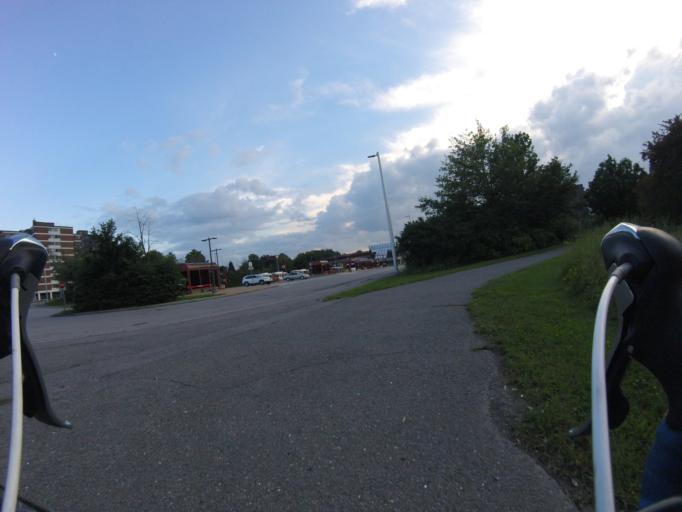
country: CA
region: Ontario
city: Bells Corners
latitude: 45.3667
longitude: -75.7813
